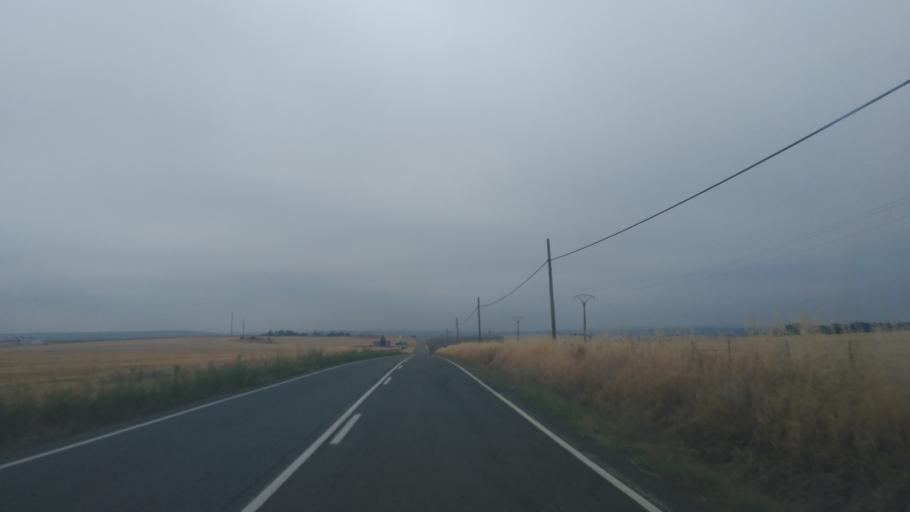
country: ES
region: Castille and Leon
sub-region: Provincia de Salamanca
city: Matilla de los Canos del Rio
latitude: 40.8394
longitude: -5.9485
